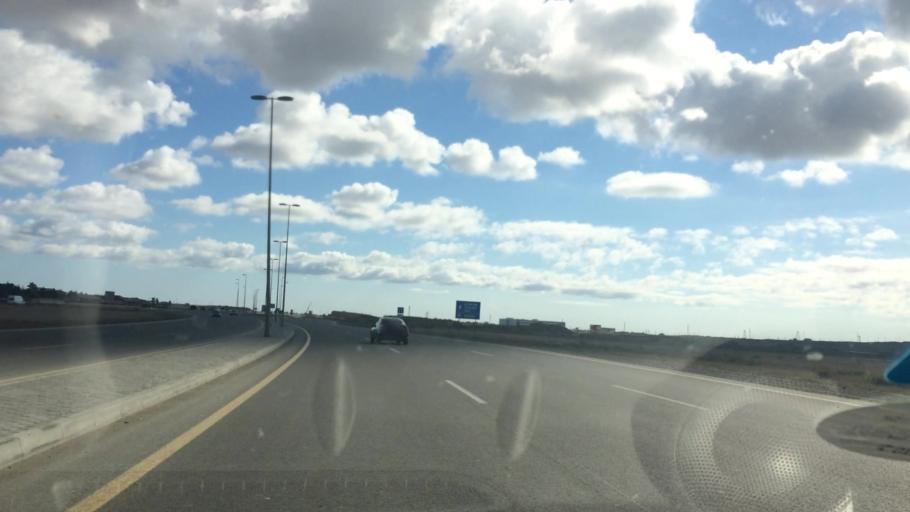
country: AZ
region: Baki
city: Mardakyany
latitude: 40.4587
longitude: 50.1293
